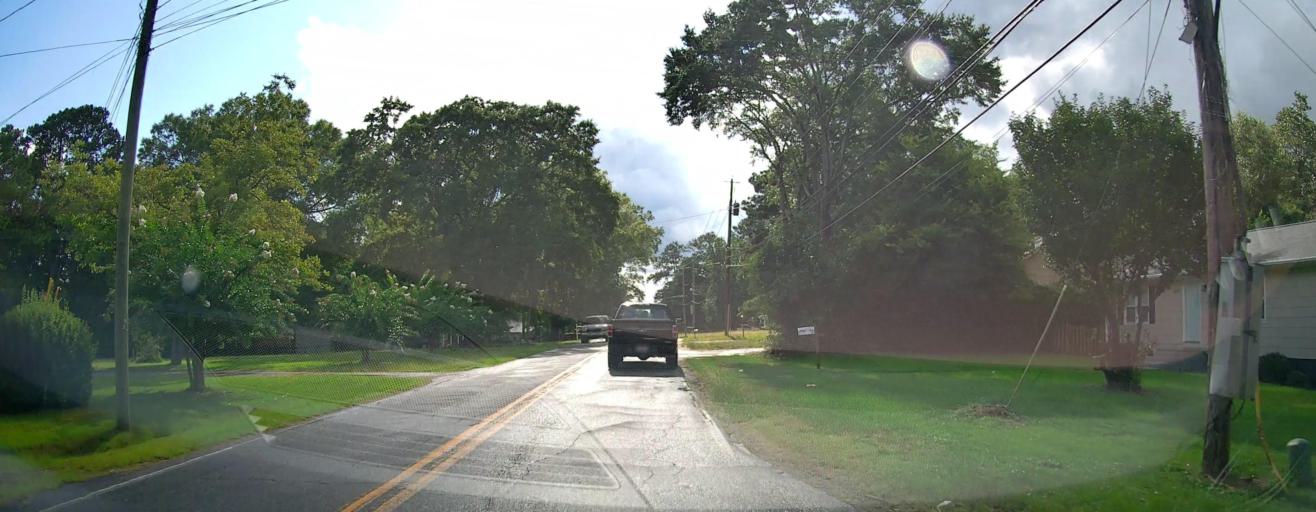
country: US
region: Alabama
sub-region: Russell County
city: Phenix City
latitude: 32.5224
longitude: -84.9730
